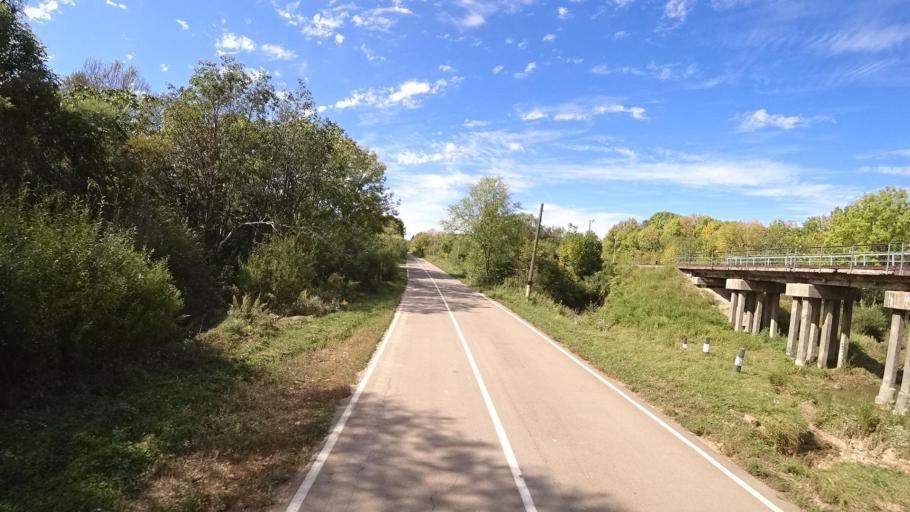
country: RU
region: Primorskiy
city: Yakovlevka
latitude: 44.3937
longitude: 133.6069
